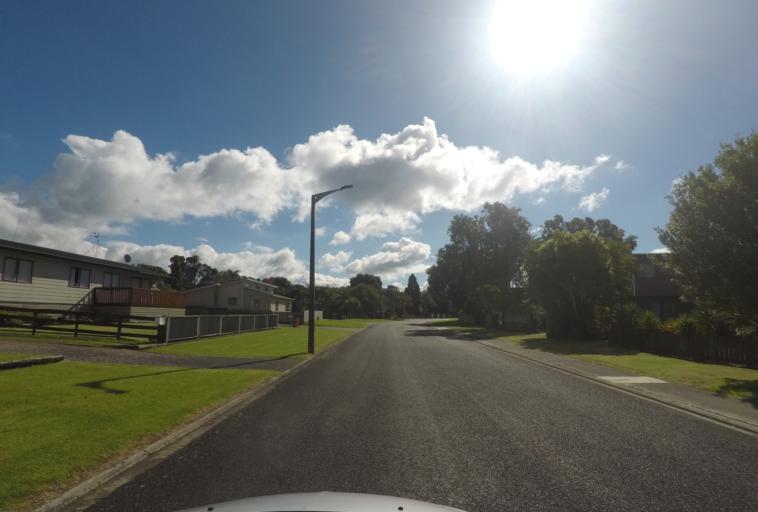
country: NZ
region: Bay of Plenty
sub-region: Western Bay of Plenty District
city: Waihi Beach
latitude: -37.4158
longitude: 175.9436
